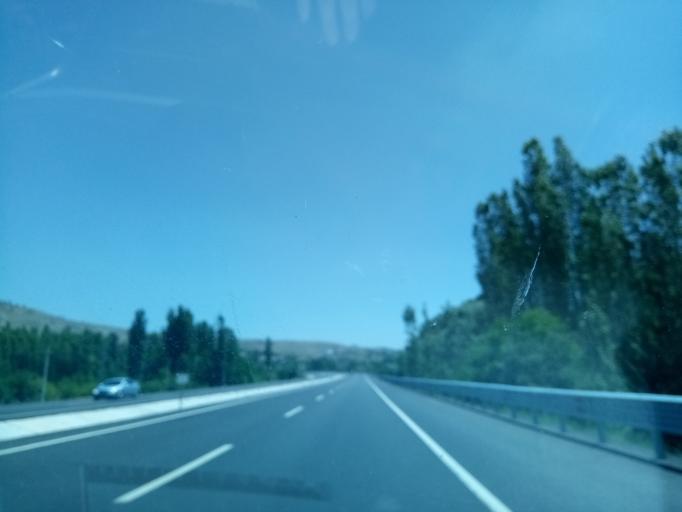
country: TR
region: Konya
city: Kiziloren
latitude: 37.7509
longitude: 32.1689
